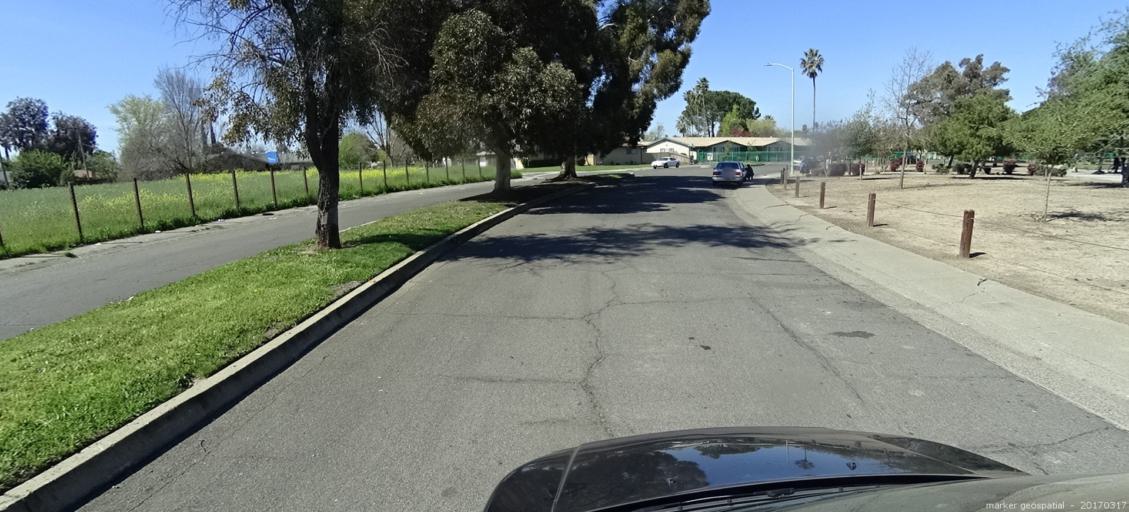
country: US
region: California
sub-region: Sacramento County
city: Parkway
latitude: 38.4917
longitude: -121.4819
